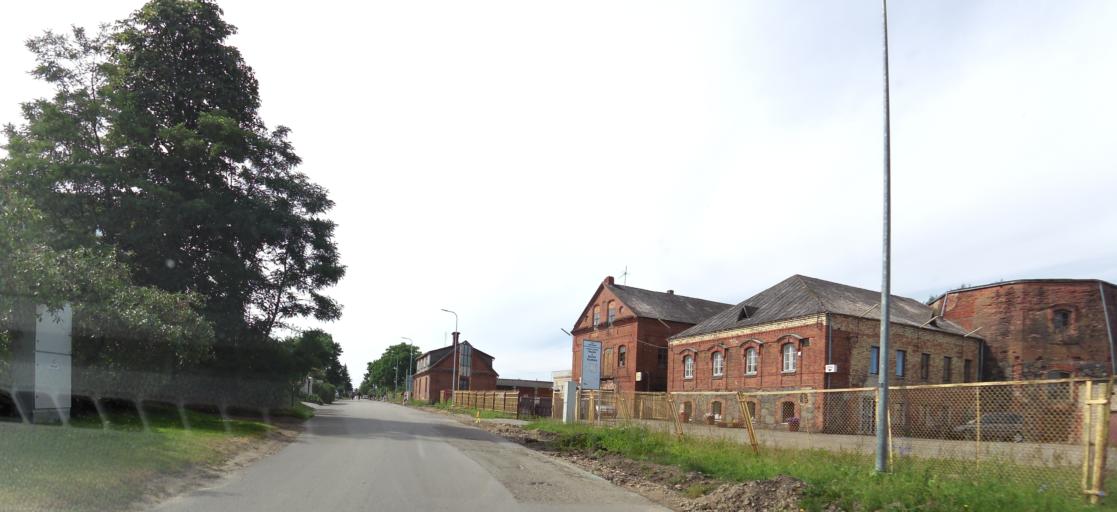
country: LT
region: Panevezys
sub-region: Birzai
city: Birzai
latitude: 56.2076
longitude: 24.7671
